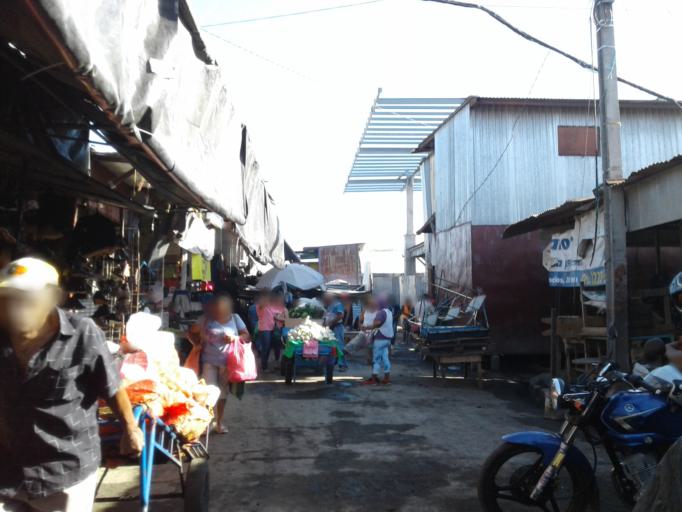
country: NI
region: Managua
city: Managua
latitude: 12.1479
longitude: -86.2609
